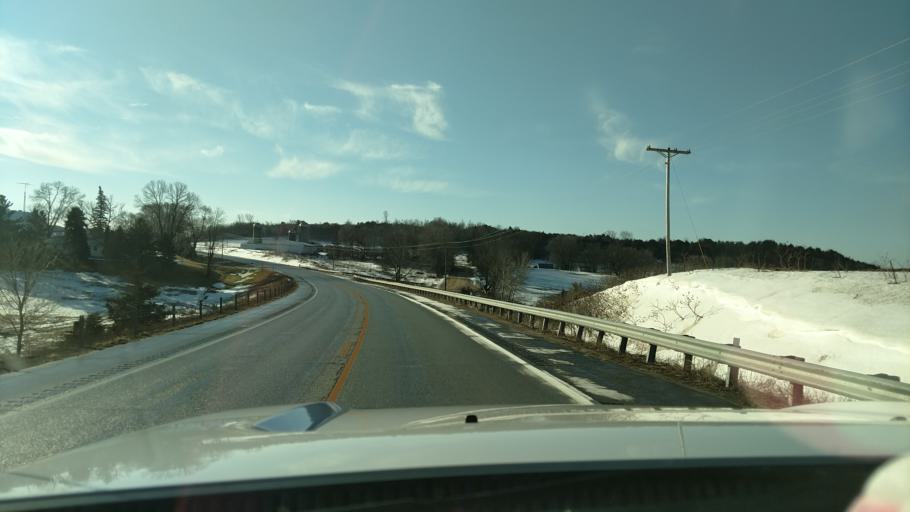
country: US
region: Minnesota
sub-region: Olmsted County
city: Oronoco
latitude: 44.1499
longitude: -92.4193
